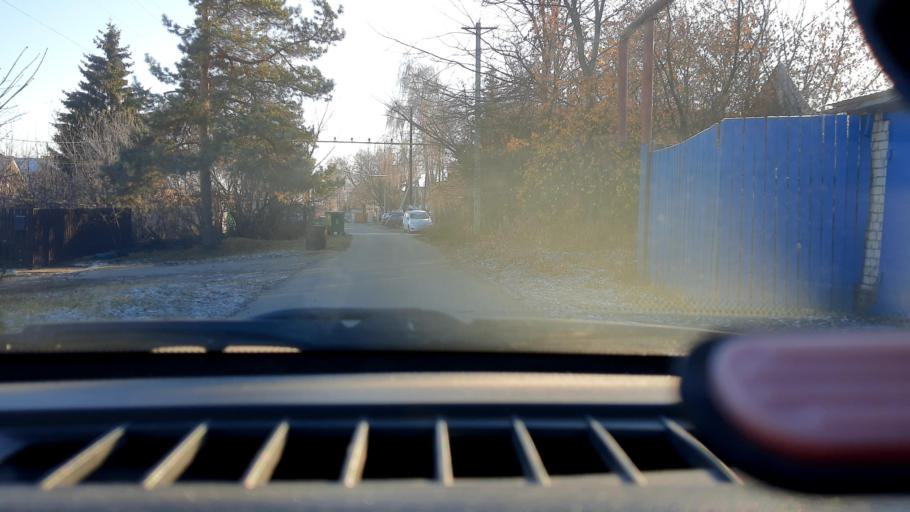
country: RU
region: Nizjnij Novgorod
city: Afonino
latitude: 56.3050
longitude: 44.0901
